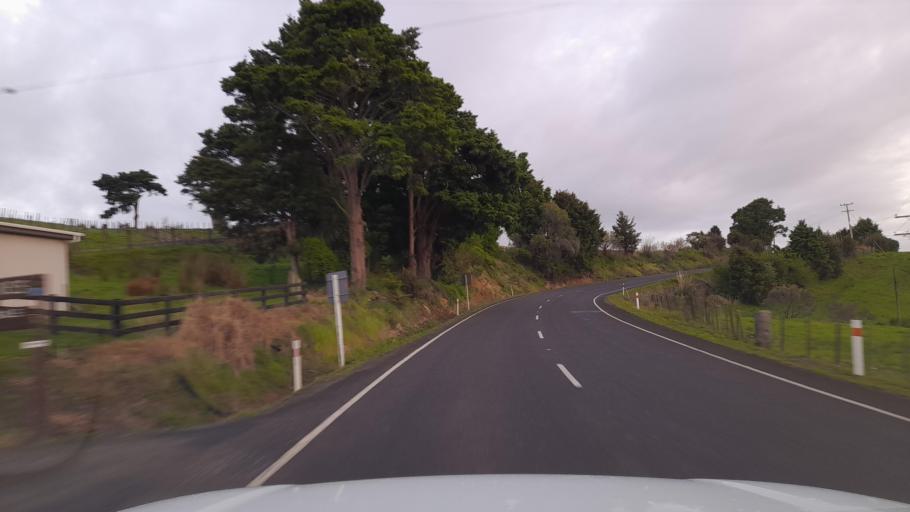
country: NZ
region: Northland
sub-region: Whangarei
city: Maungatapere
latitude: -35.7311
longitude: 174.0464
